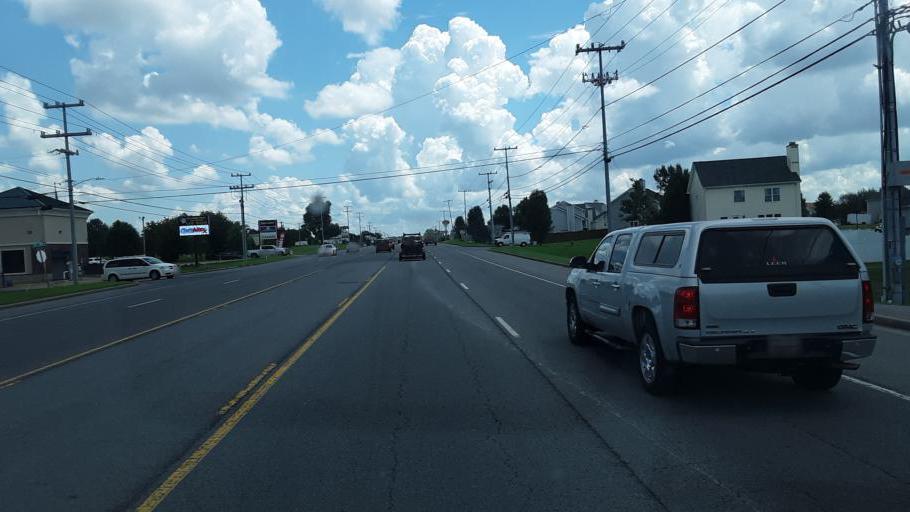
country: US
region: Tennessee
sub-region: Montgomery County
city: Clarksville
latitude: 36.6266
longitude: -87.3301
